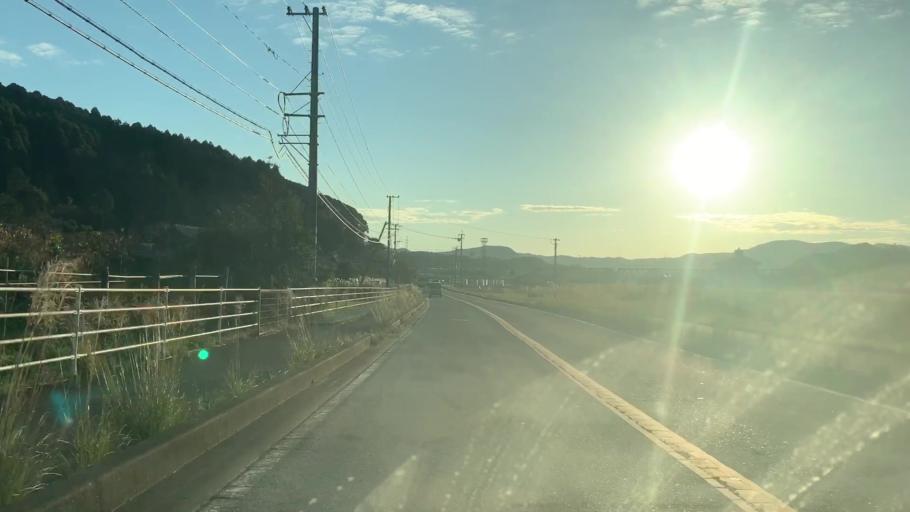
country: JP
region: Saga Prefecture
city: Karatsu
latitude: 33.3586
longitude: 130.0074
